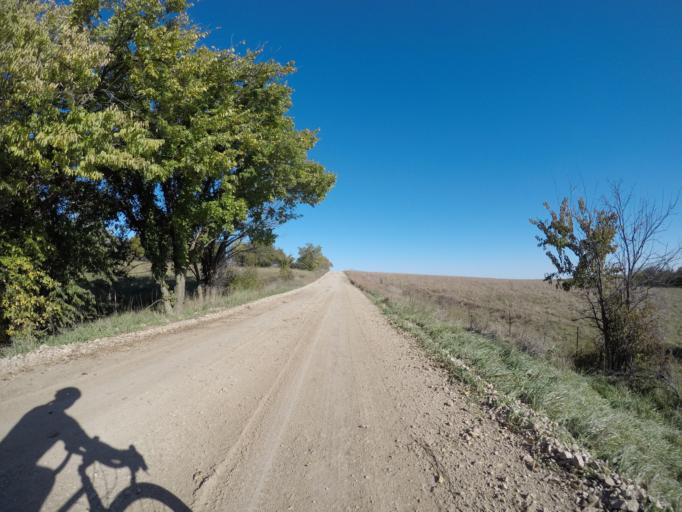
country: US
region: Kansas
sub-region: Wabaunsee County
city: Alma
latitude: 38.8741
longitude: -96.4097
